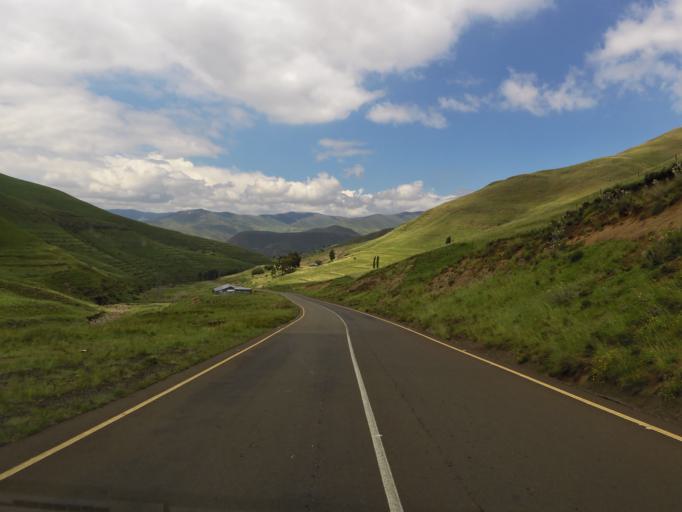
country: LS
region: Butha-Buthe
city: Butha-Buthe
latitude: -29.1106
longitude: 28.4585
